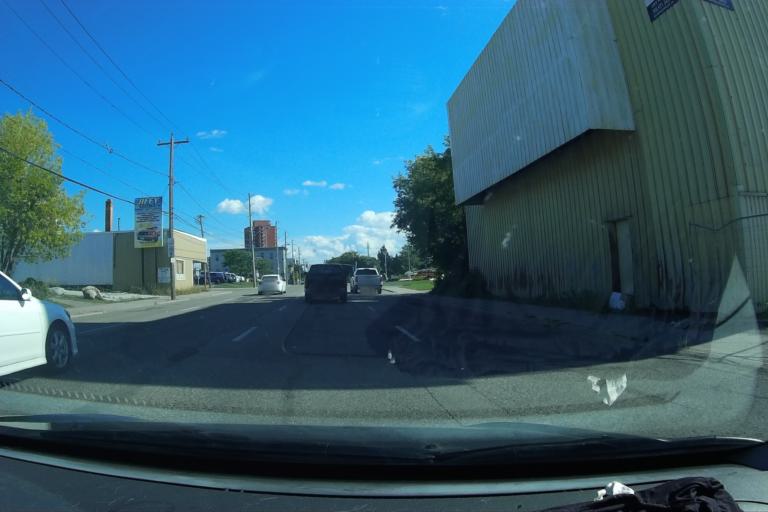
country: CA
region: Ontario
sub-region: Algoma
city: Sault Ste. Marie
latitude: 46.5093
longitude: -84.3325
